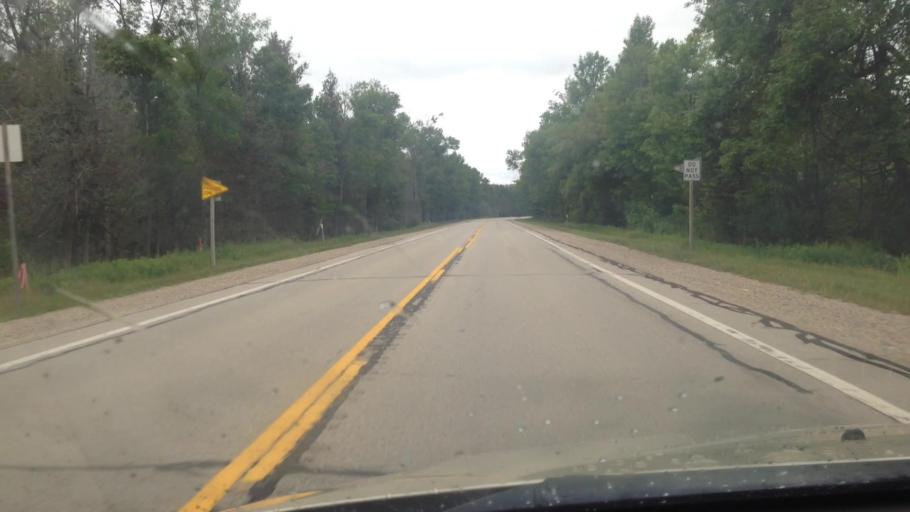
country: US
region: Michigan
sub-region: Menominee County
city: Menominee
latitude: 45.4229
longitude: -87.3487
